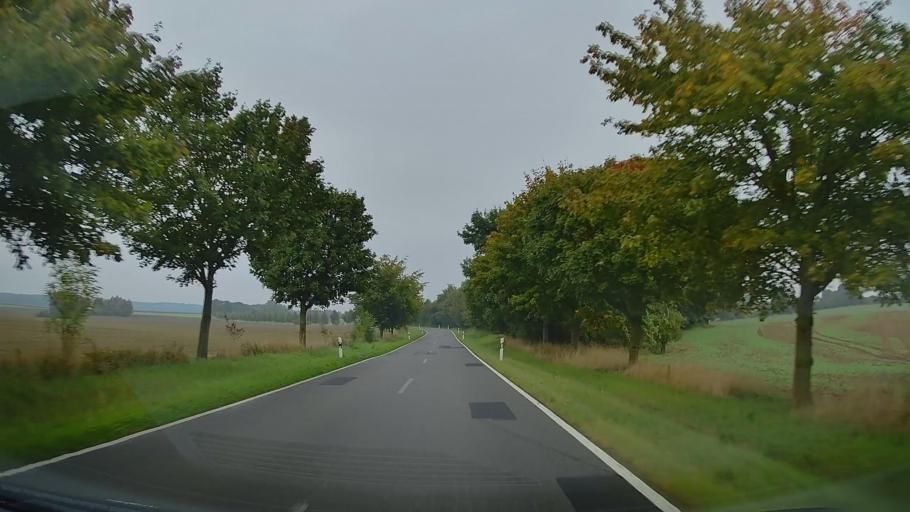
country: DE
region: Mecklenburg-Vorpommern
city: Kalkhorst
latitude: 53.9808
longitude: 11.0485
